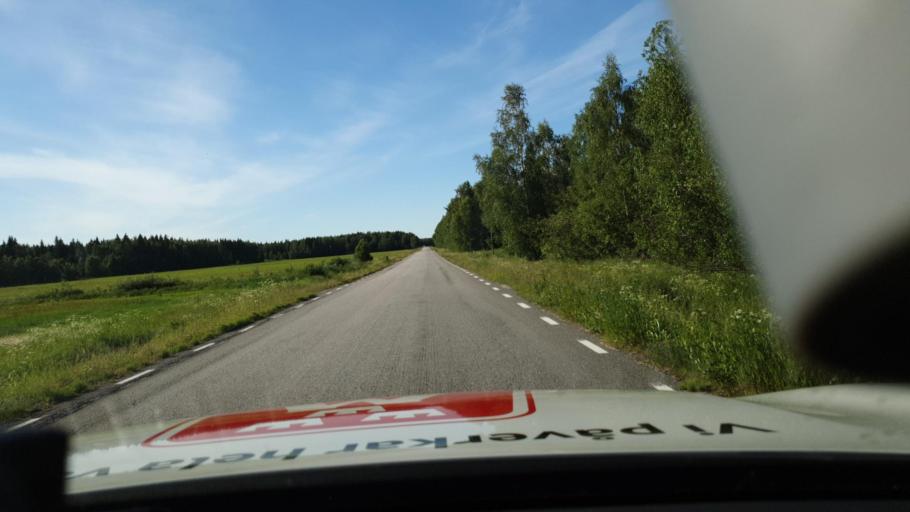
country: SE
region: Norrbotten
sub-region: Kalix Kommun
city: Toere
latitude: 65.8730
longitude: 22.6735
